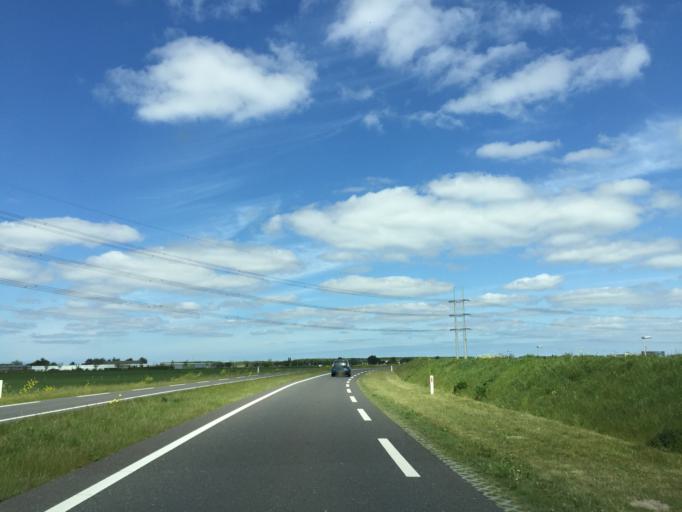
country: NL
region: South Holland
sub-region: Gemeente Lansingerland
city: Berkel en Rodenrijs
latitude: 52.0255
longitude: 4.4729
